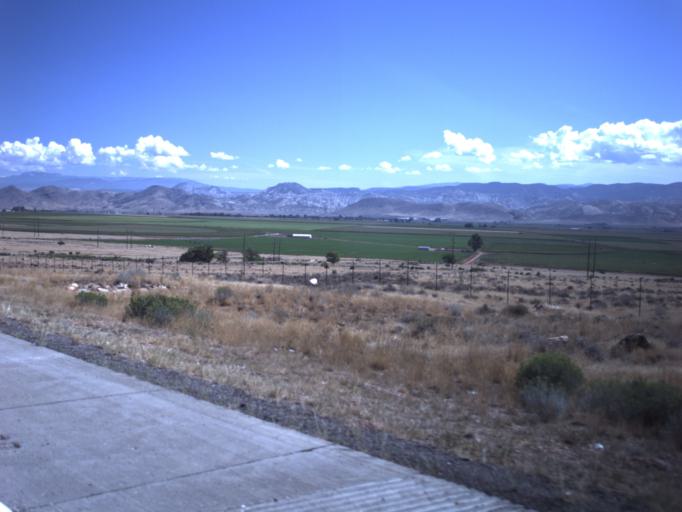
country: US
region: Utah
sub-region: Sevier County
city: Richfield
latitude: 38.8265
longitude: -112.0395
